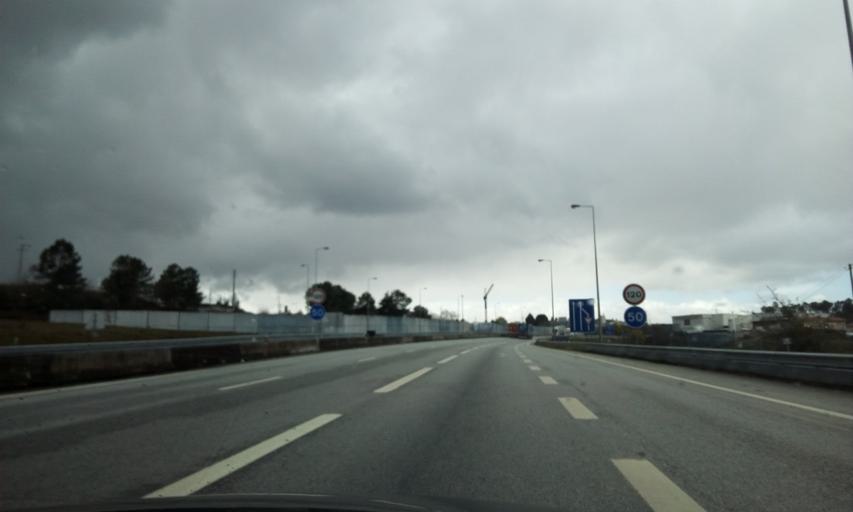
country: PT
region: Viseu
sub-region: Viseu
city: Rio de Loba
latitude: 40.6385
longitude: -7.8514
